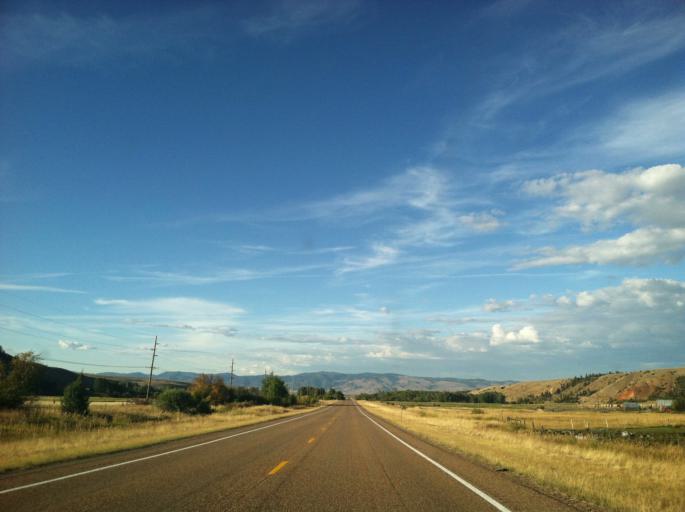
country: US
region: Montana
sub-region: Granite County
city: Philipsburg
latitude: 46.5205
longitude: -113.2262
